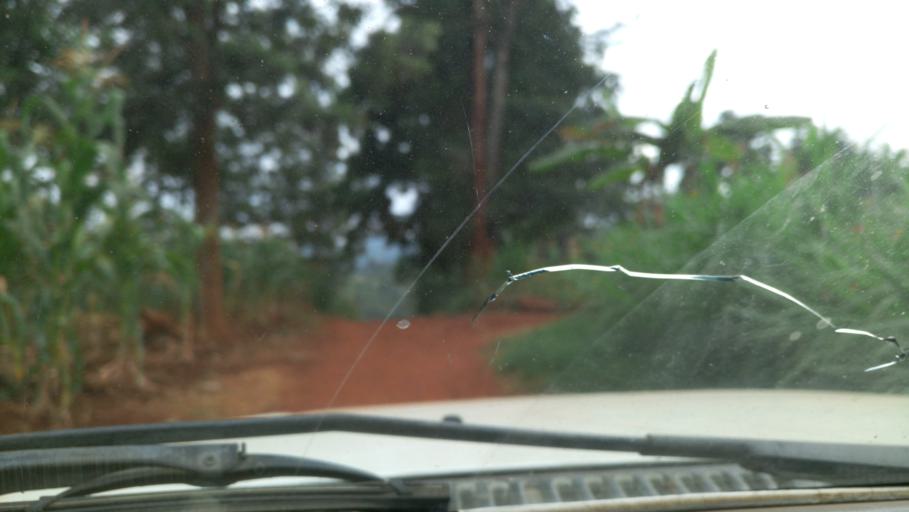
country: KE
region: Murang'a District
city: Murang'a
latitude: -0.7079
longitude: 37.1385
